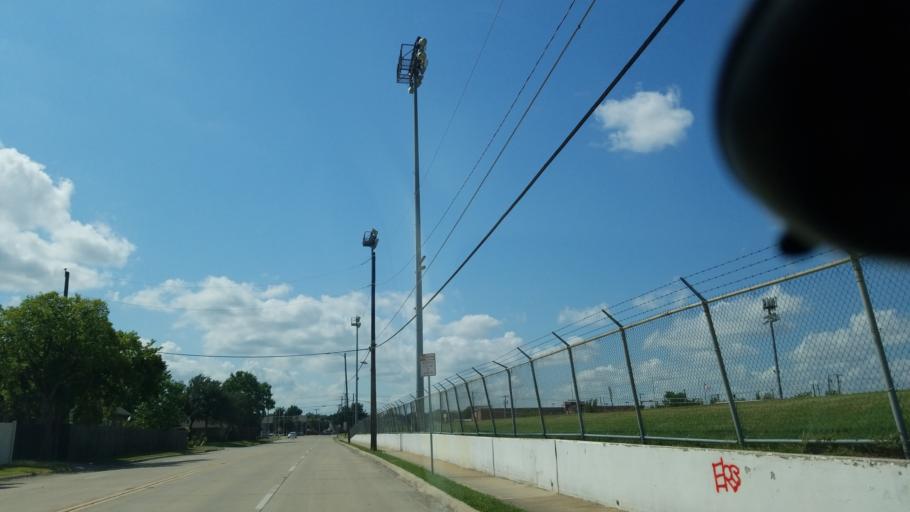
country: US
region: Texas
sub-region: Dallas County
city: Grand Prairie
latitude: 32.7123
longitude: -96.9988
